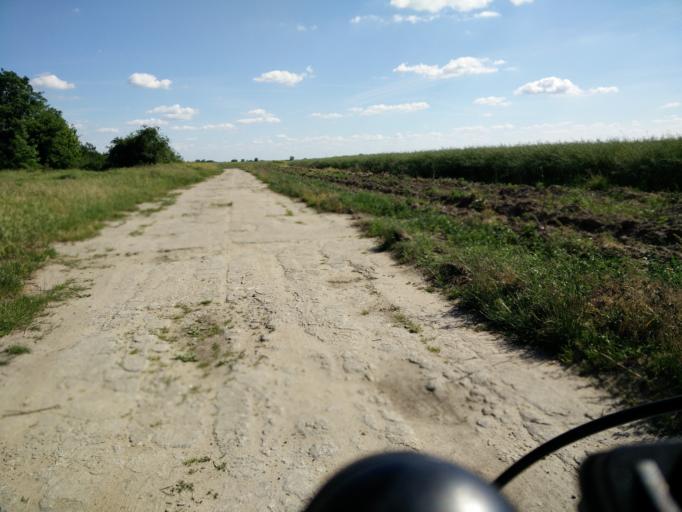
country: PL
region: Greater Poland Voivodeship
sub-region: Powiat sredzki
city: Sroda Wielkopolska
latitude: 52.2501
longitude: 17.3179
